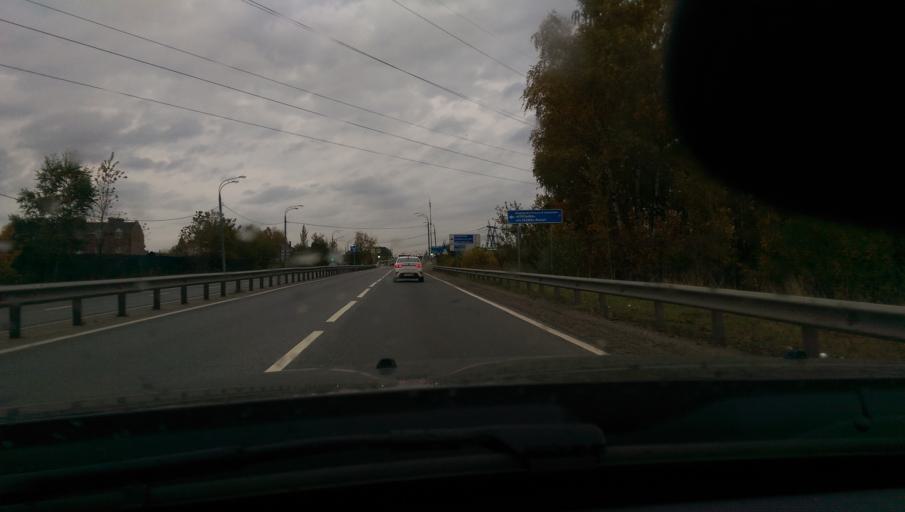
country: RU
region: Moskovskaya
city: Povedniki
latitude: 55.9523
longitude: 37.6507
